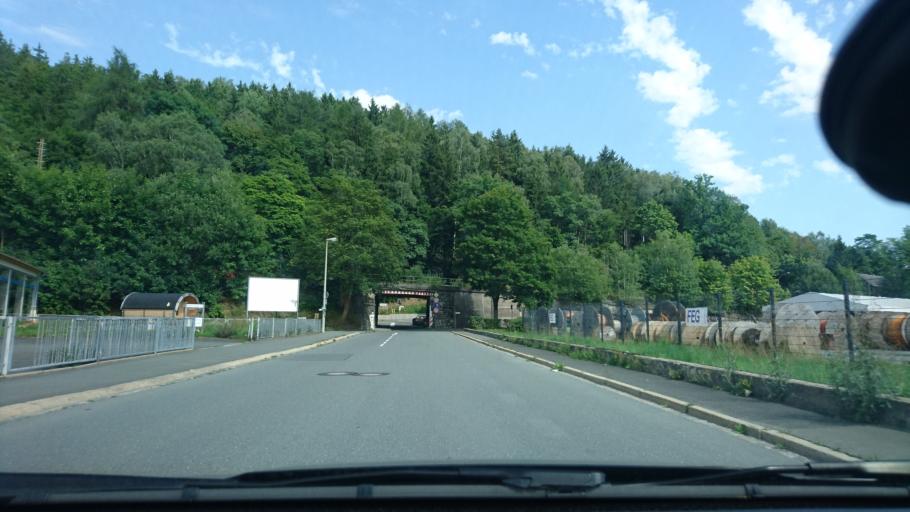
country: DE
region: Bavaria
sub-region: Upper Franconia
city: Naila
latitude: 50.3261
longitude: 11.7158
